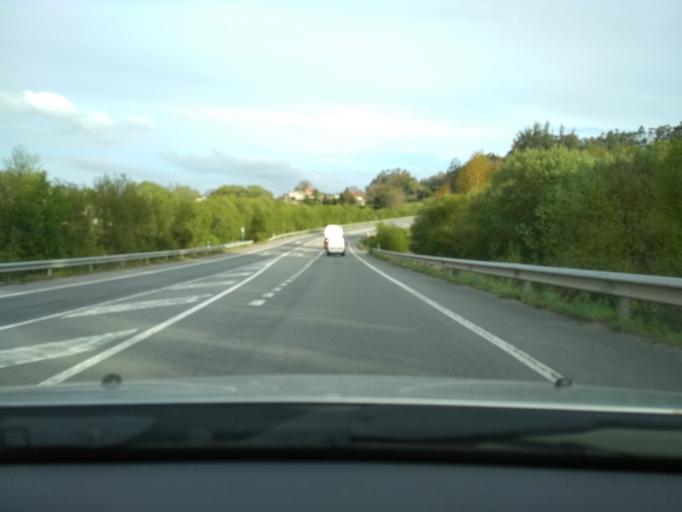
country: ES
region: Galicia
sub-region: Provincia da Coruna
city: Cerceda
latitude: 43.2189
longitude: -8.4574
